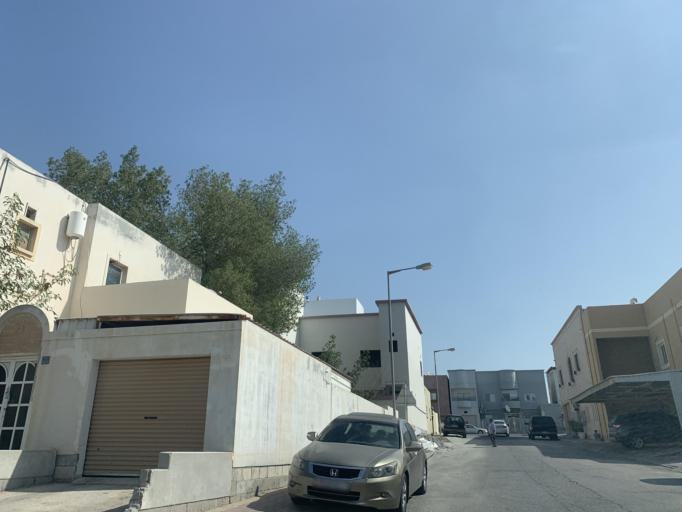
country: BH
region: Central Governorate
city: Madinat Hamad
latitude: 26.1316
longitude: 50.5011
